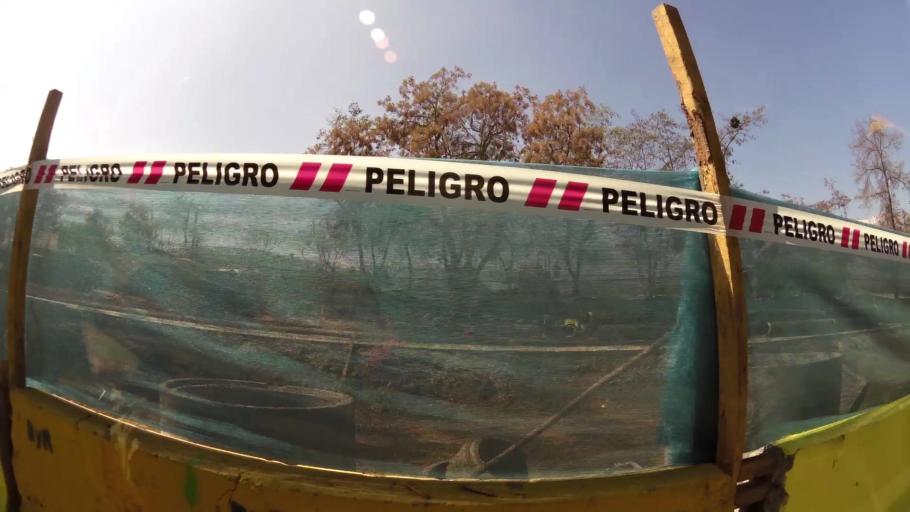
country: CL
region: Santiago Metropolitan
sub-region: Provincia de Santiago
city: Villa Presidente Frei, Nunoa, Santiago, Chile
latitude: -33.4170
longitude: -70.5387
